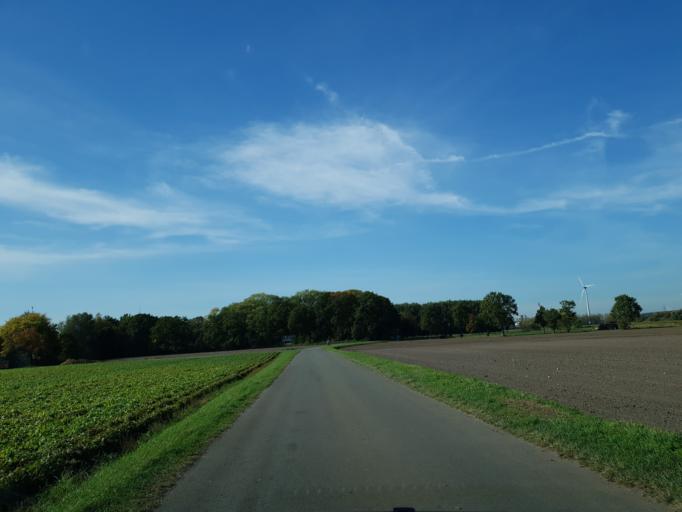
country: BE
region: Flanders
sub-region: Provincie Antwerpen
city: Stabroek
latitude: 51.3628
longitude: 4.3194
